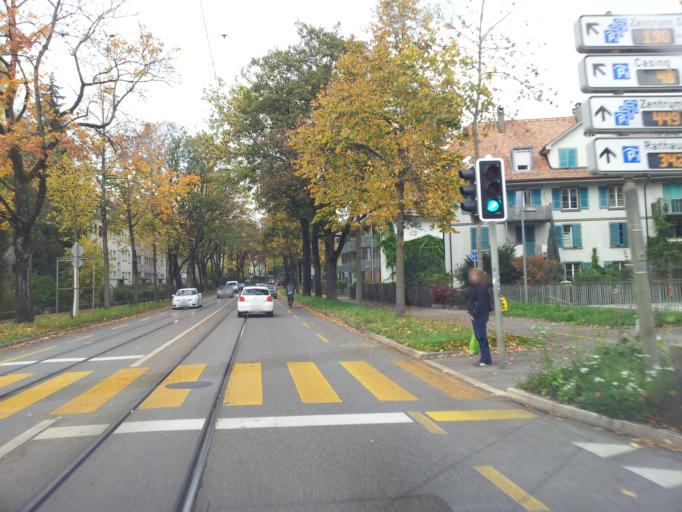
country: CH
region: Bern
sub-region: Bern-Mittelland District
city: Muri
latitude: 46.9396
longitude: 7.4702
